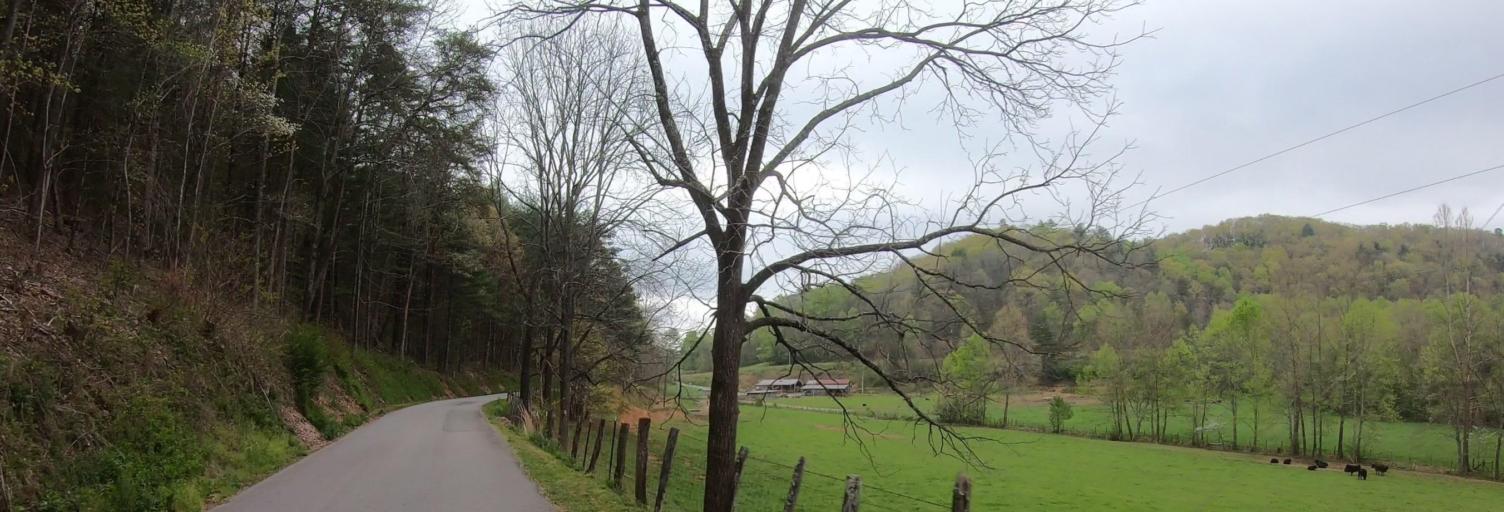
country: US
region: Georgia
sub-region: Union County
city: Blairsville
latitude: 34.7923
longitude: -83.9083
